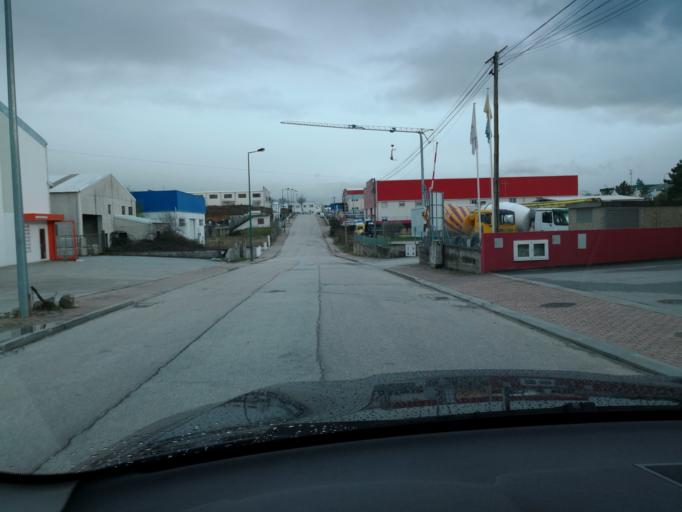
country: PT
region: Vila Real
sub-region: Vila Real
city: Vila Real
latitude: 41.2791
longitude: -7.7089
